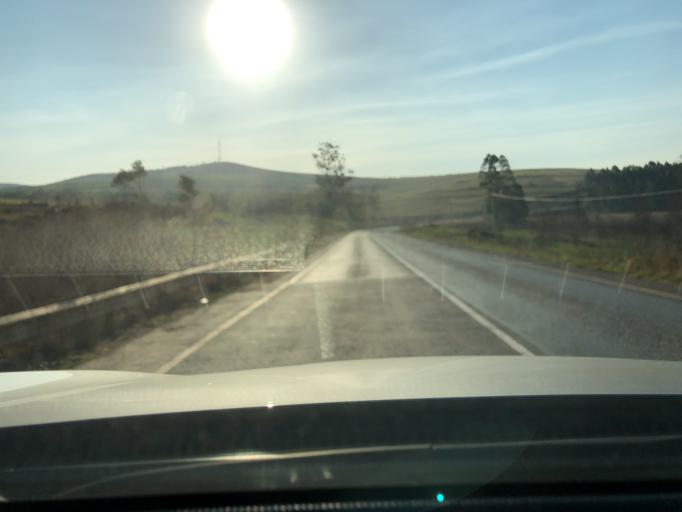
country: ZA
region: KwaZulu-Natal
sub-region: Sisonke District Municipality
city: Ixopo
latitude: -30.2573
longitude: 30.1904
